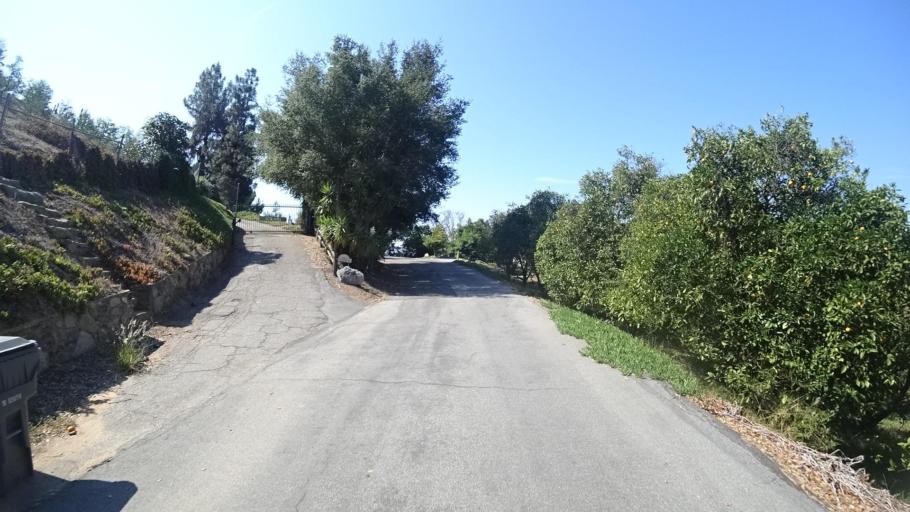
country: US
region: California
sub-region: San Diego County
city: Valley Center
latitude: 33.3431
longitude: -117.0057
